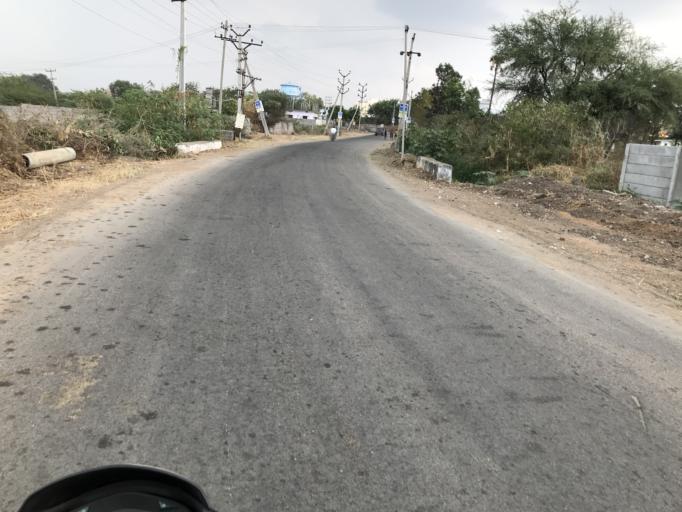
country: IN
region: Telangana
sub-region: Rangareddi
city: Lal Bahadur Nagar
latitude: 17.2853
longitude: 78.6336
